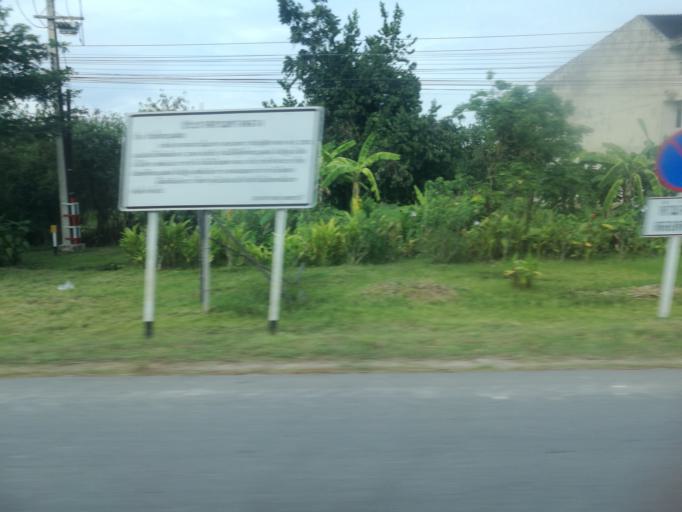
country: TH
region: Phetchaburi
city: Cha-am
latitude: 12.7997
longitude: 99.9416
